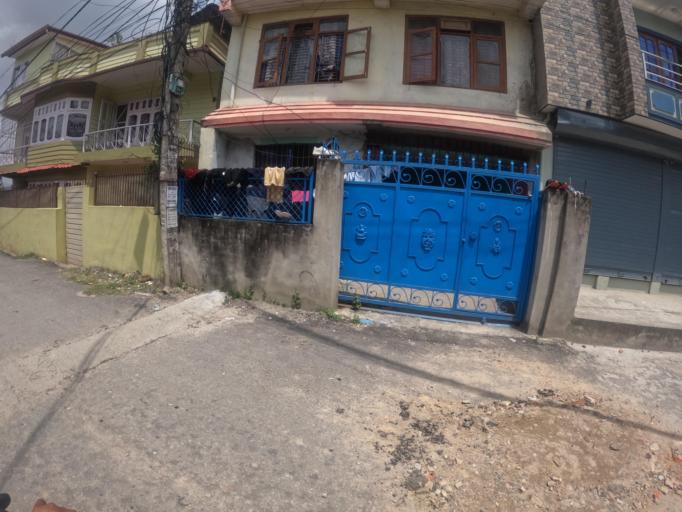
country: NP
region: Central Region
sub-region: Bagmati Zone
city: Bhaktapur
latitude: 27.6765
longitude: 85.3733
